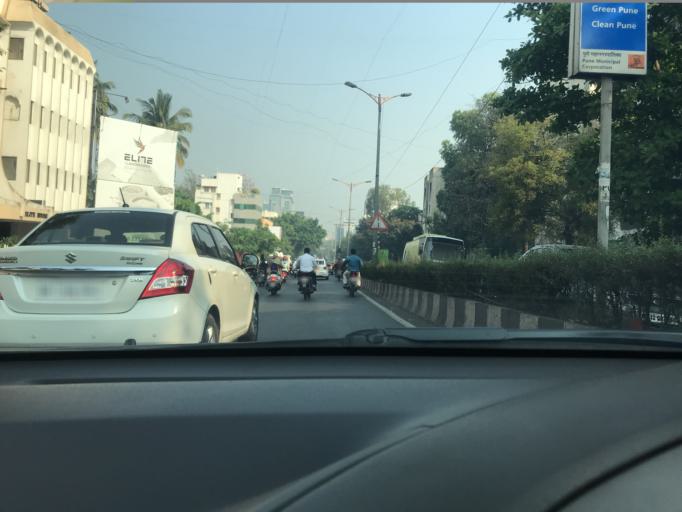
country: IN
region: Maharashtra
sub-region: Pune Division
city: Shivaji Nagar
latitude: 18.5256
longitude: 73.8297
